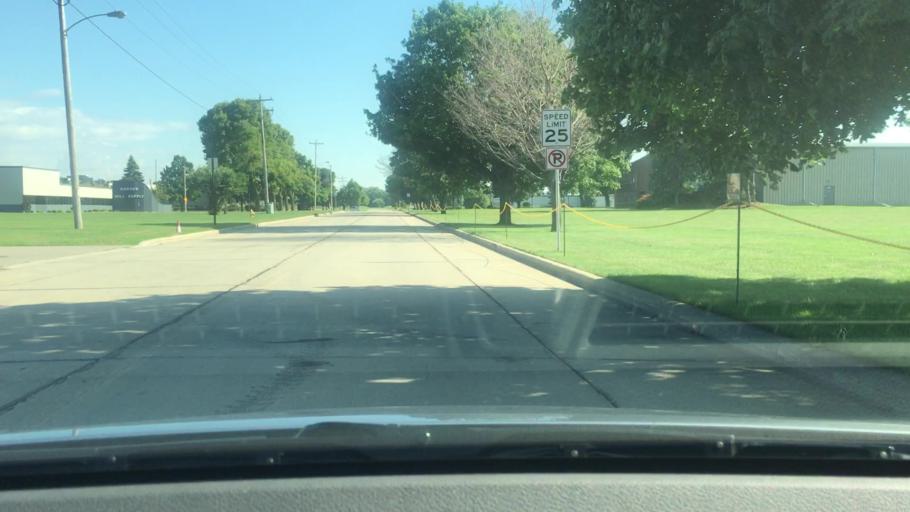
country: US
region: Wisconsin
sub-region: Winnebago County
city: Oshkosh
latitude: 43.9798
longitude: -88.5506
